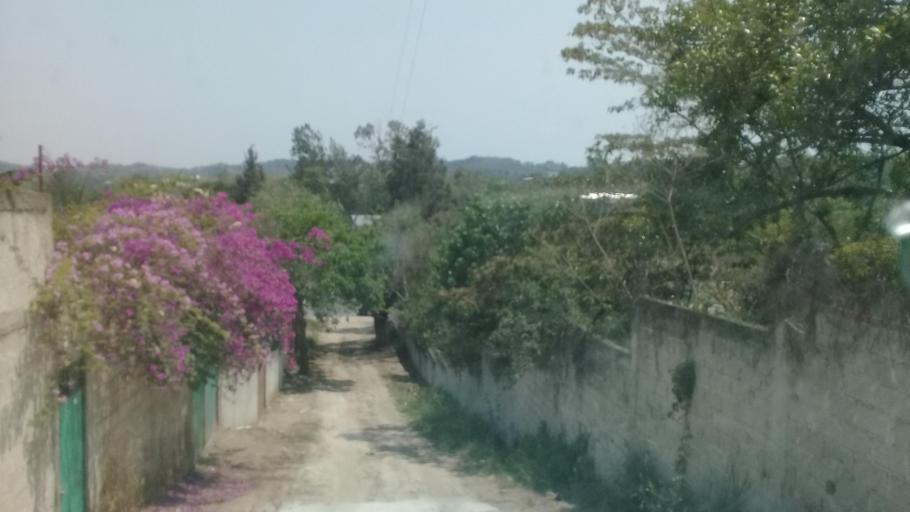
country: MX
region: Veracruz
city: El Castillo
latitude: 19.5536
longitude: -96.8589
